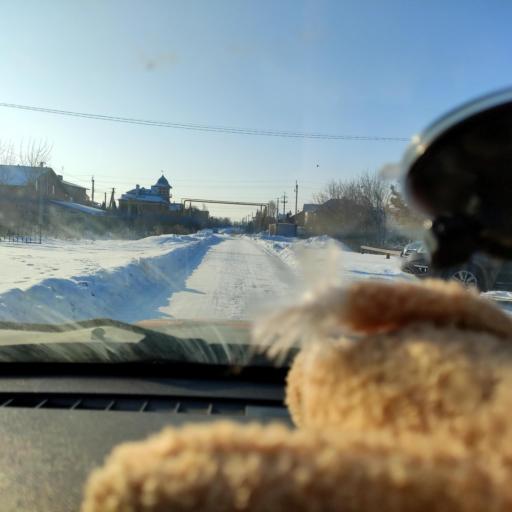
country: RU
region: Samara
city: Podstepki
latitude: 53.5171
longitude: 49.1665
